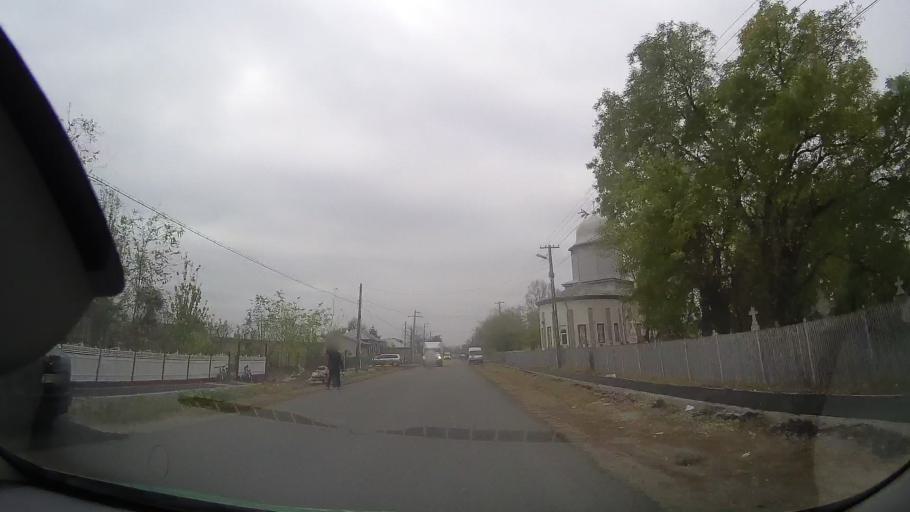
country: RO
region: Buzau
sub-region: Comuna Pogoanele
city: Pogoanele
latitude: 44.9247
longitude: 26.9951
